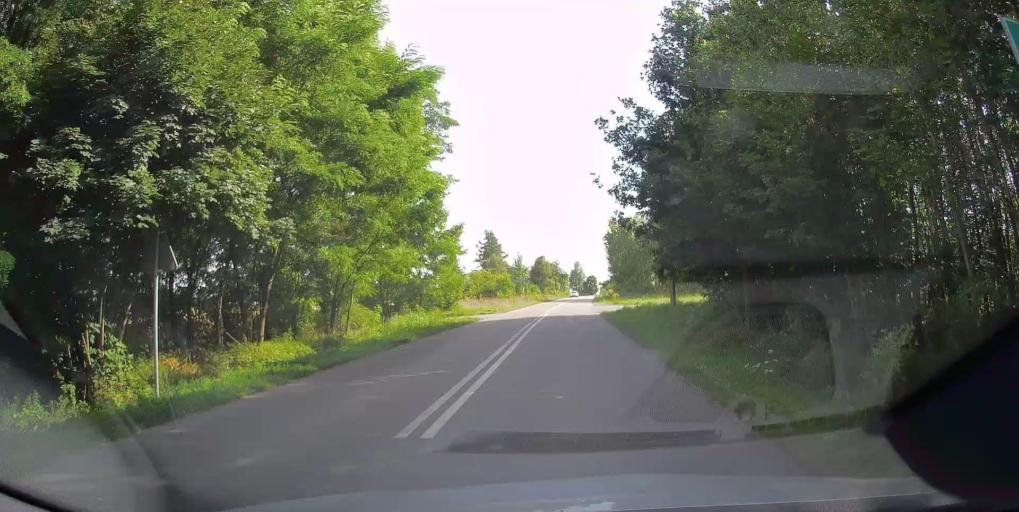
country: PL
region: Lodz Voivodeship
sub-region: Powiat opoczynski
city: Mniszkow
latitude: 51.3897
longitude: 20.0350
